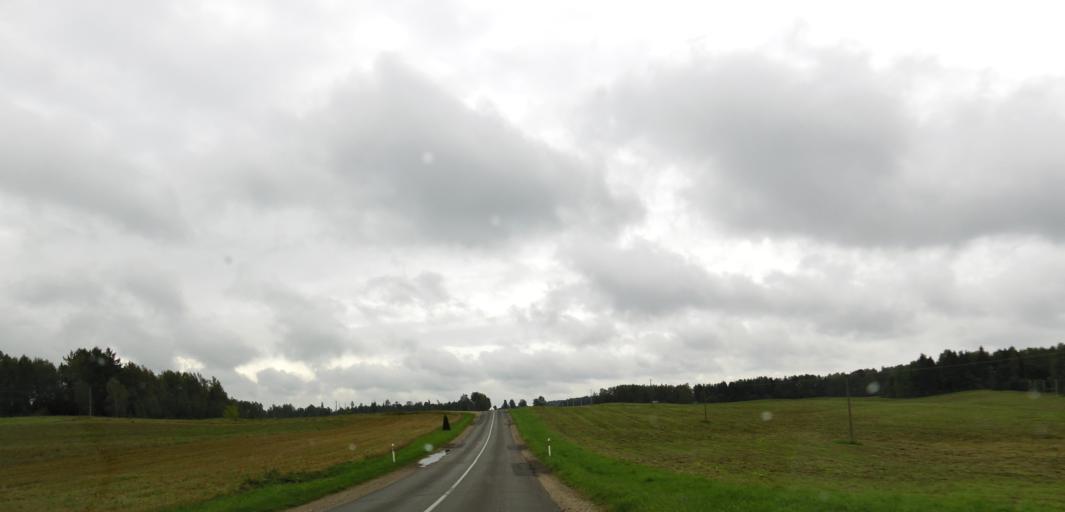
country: LT
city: Moletai
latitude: 55.2875
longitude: 25.3472
